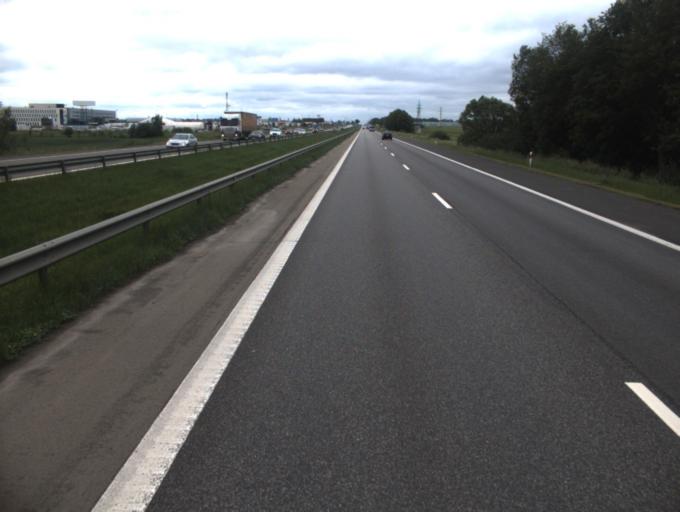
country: LT
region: Kauno apskritis
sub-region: Kaunas
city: Sargenai
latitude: 54.9702
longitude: 23.8569
